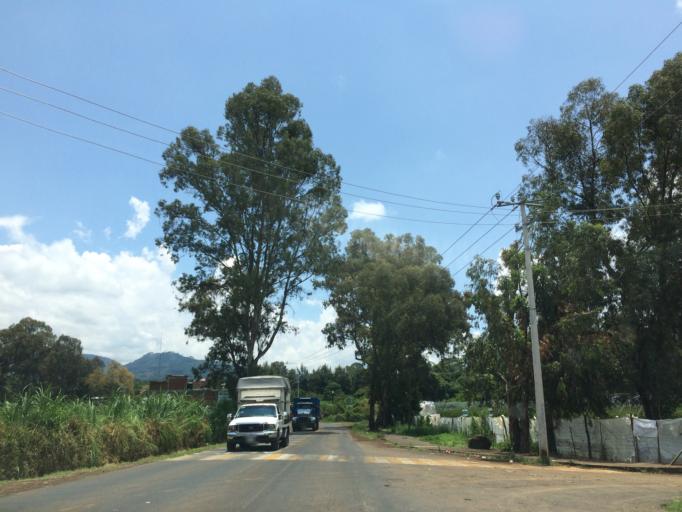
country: MX
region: Michoacan
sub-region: Periban
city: San Francisco Periban
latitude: 19.5498
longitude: -102.4004
